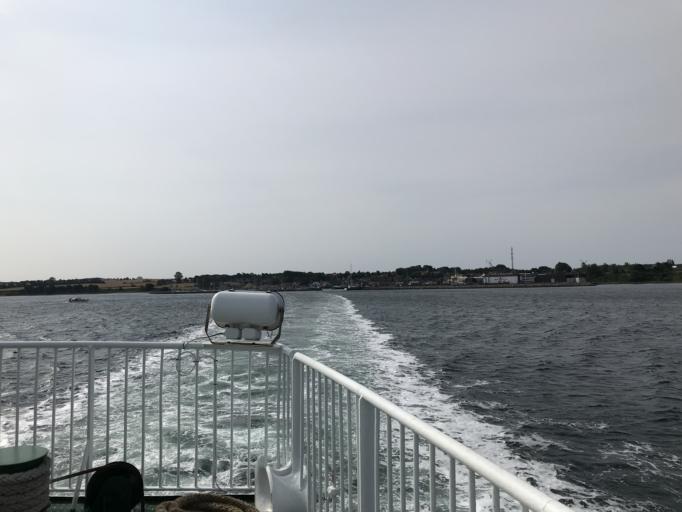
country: DK
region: South Denmark
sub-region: Faaborg-Midtfyn Kommune
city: Faaborg
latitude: 54.9474
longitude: 10.2582
